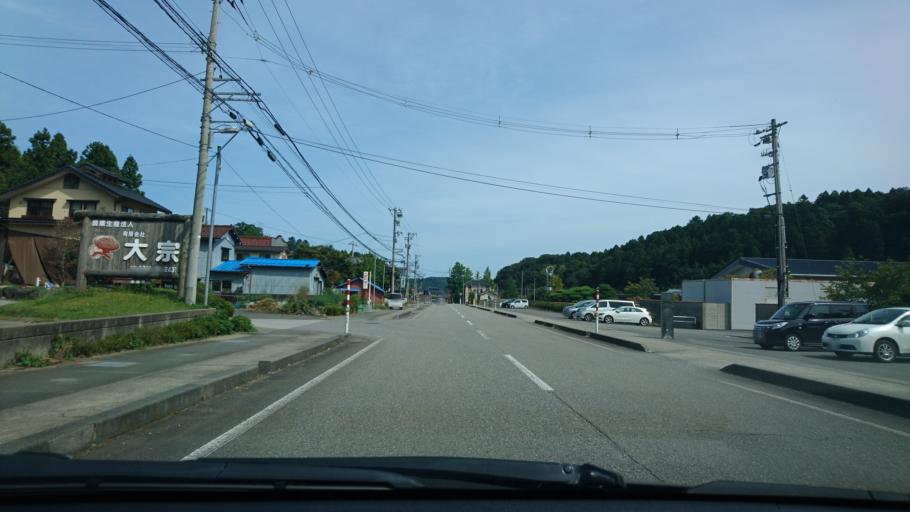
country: JP
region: Fukui
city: Maruoka
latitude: 36.2994
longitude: 136.3014
